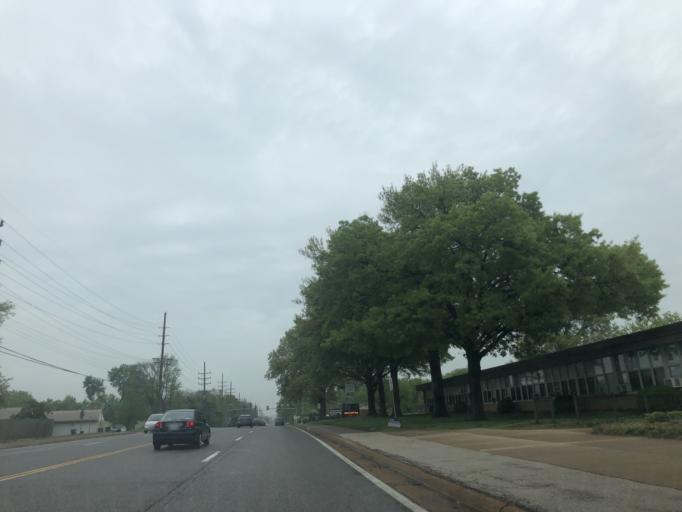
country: US
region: Missouri
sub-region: Saint Louis County
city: Marlborough
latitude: 38.5679
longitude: -90.3205
